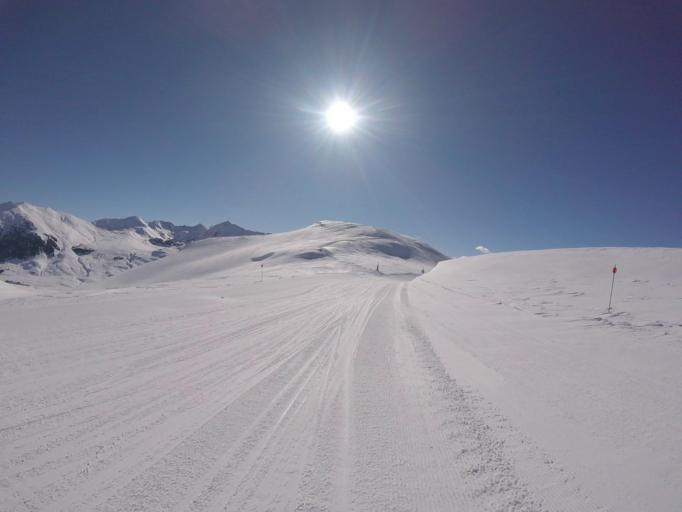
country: ES
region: Catalonia
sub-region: Provincia de Lleida
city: Vielha
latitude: 42.7285
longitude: 0.9394
